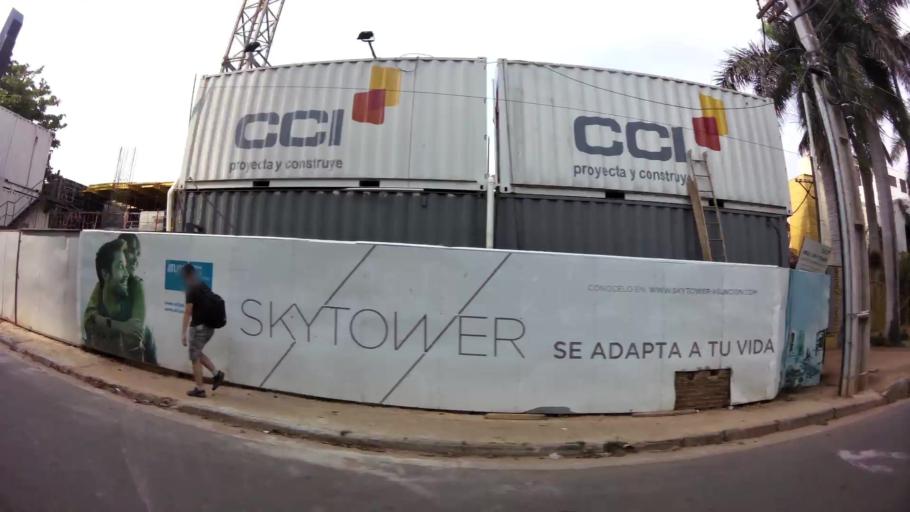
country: PY
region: Central
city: Fernando de la Mora
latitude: -25.2874
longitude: -57.5564
